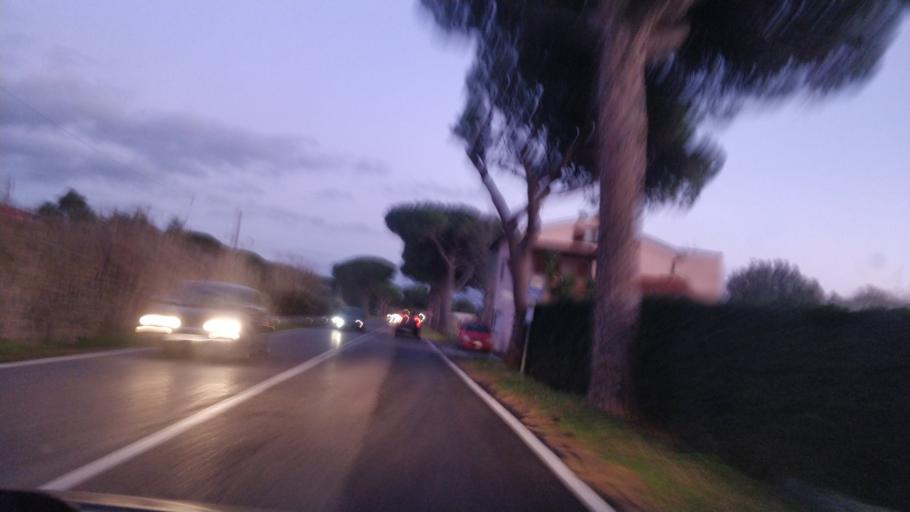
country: IT
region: Tuscany
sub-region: Provincia di Livorno
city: S.P. in Palazzi
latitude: 43.3326
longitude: 10.4961
